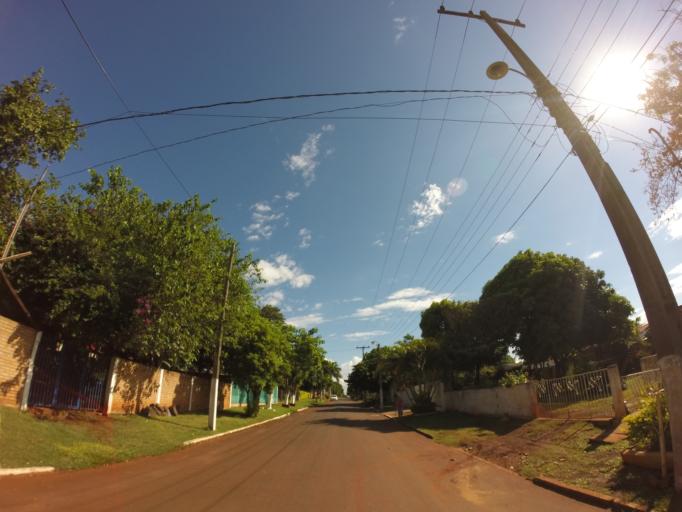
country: PY
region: Alto Parana
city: Ciudad del Este
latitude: -25.4031
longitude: -54.6250
